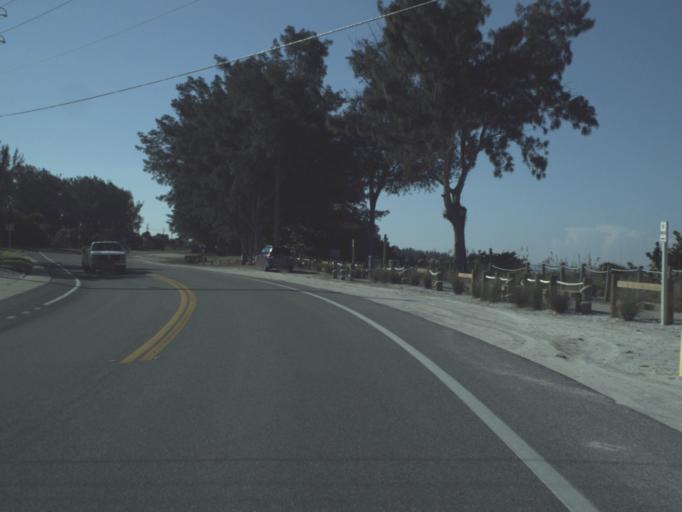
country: US
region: Florida
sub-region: Manatee County
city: Bradenton Beach
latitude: 27.4581
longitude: -82.6962
